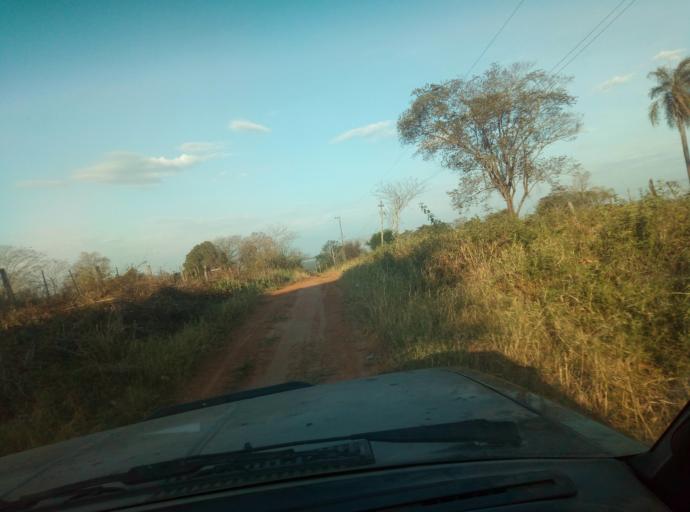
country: PY
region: Caaguazu
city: Doctor Cecilio Baez
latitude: -25.1520
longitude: -56.2473
